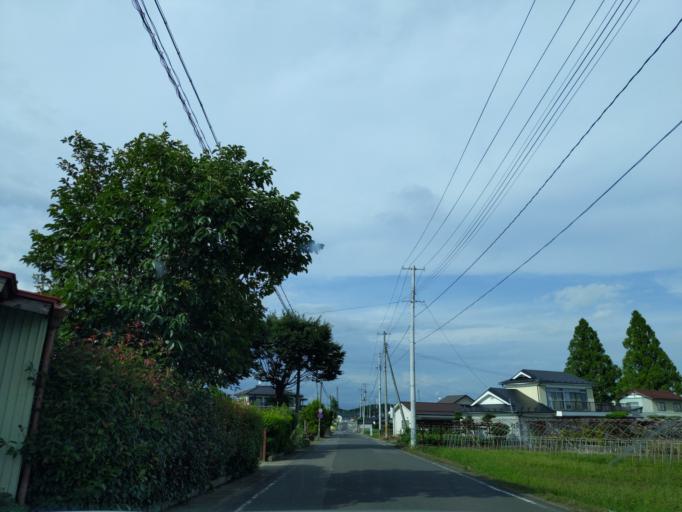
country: JP
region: Fukushima
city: Sukagawa
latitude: 37.3297
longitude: 140.3304
